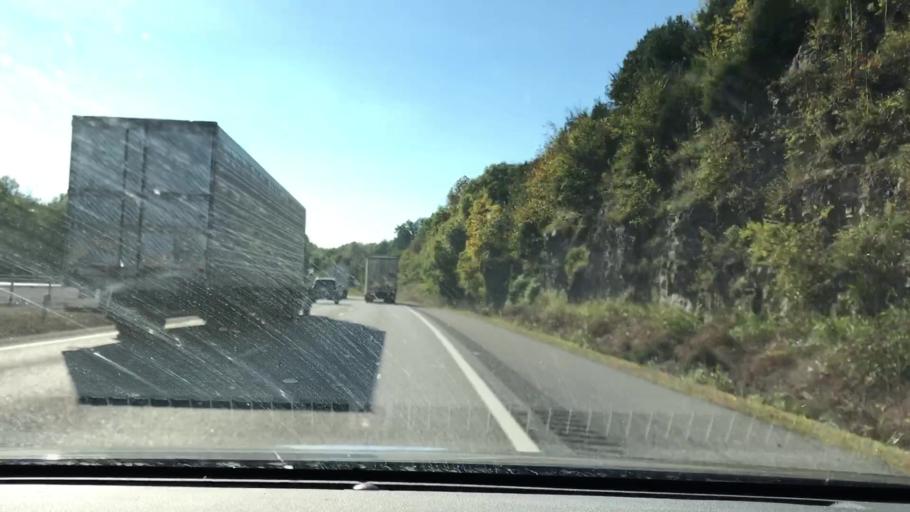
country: US
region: Tennessee
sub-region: Wilson County
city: Watertown
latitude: 36.1755
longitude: -86.0778
